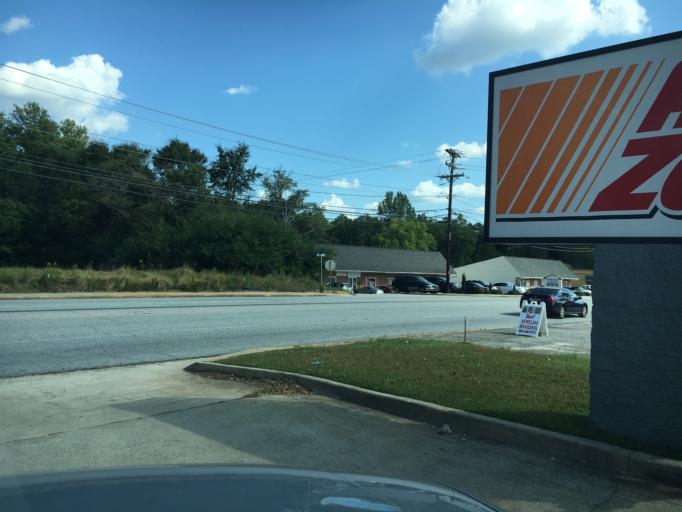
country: US
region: South Carolina
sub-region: Greenville County
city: Simpsonville
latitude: 34.7279
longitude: -82.2544
